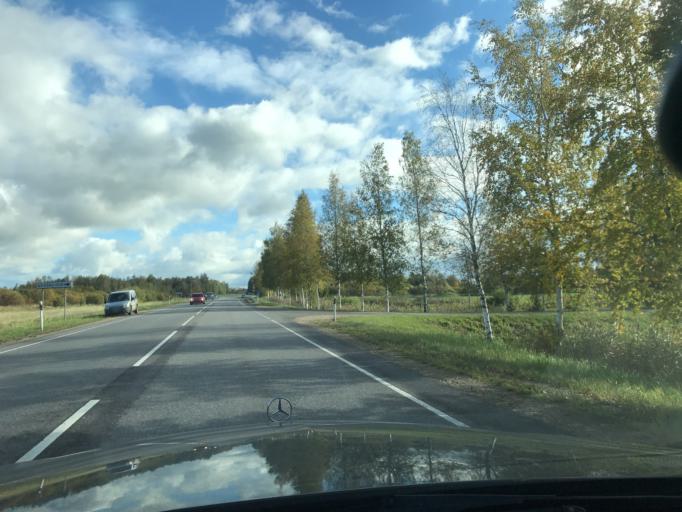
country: EE
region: Vorumaa
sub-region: Voru linn
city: Voru
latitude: 57.8604
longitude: 26.9935
